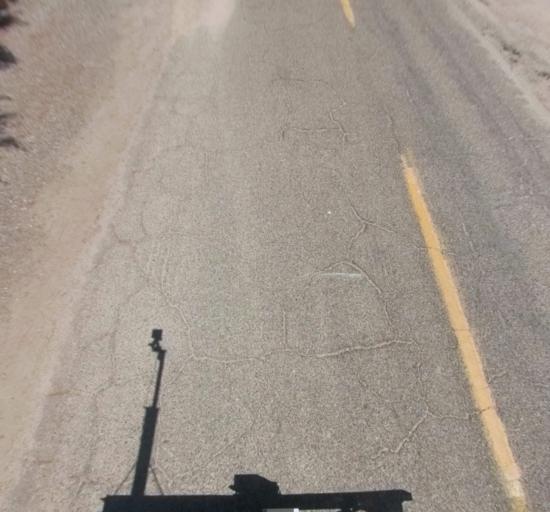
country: US
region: California
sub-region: Madera County
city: Chowchilla
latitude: 37.0803
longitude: -120.3108
